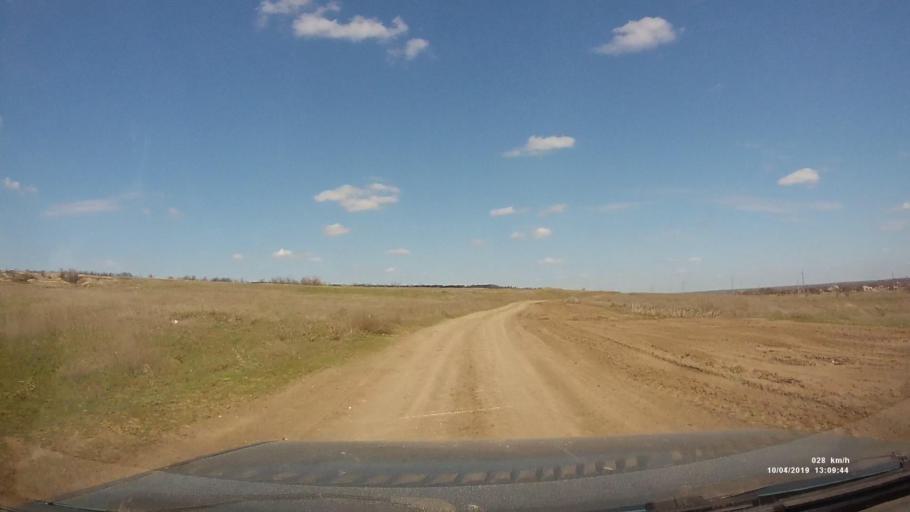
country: RU
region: Rostov
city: Masalovka
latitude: 48.4073
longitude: 40.2441
